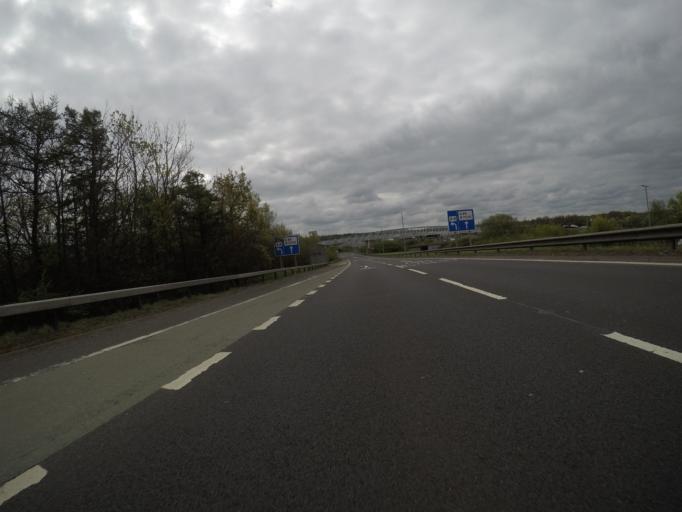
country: GB
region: Scotland
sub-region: Edinburgh
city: Newbridge
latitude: 55.9413
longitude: -3.4024
